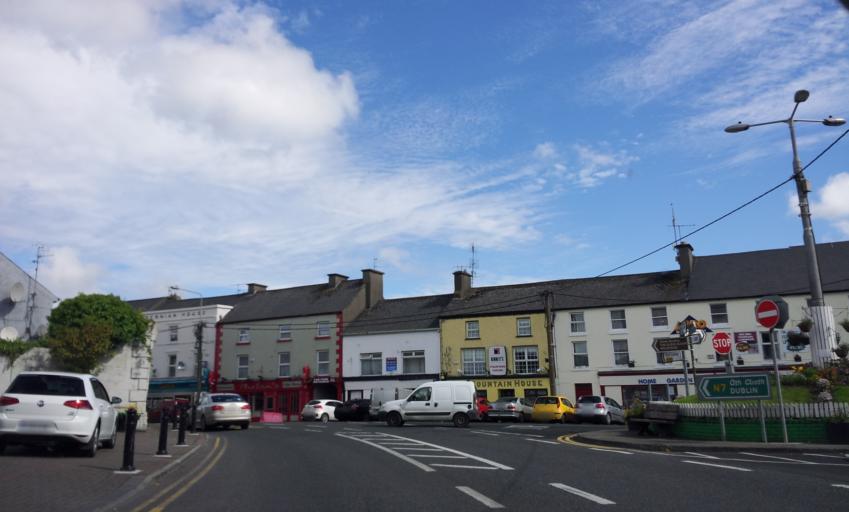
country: IE
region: Leinster
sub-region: Laois
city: Mountrath
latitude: 53.0010
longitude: -7.4747
